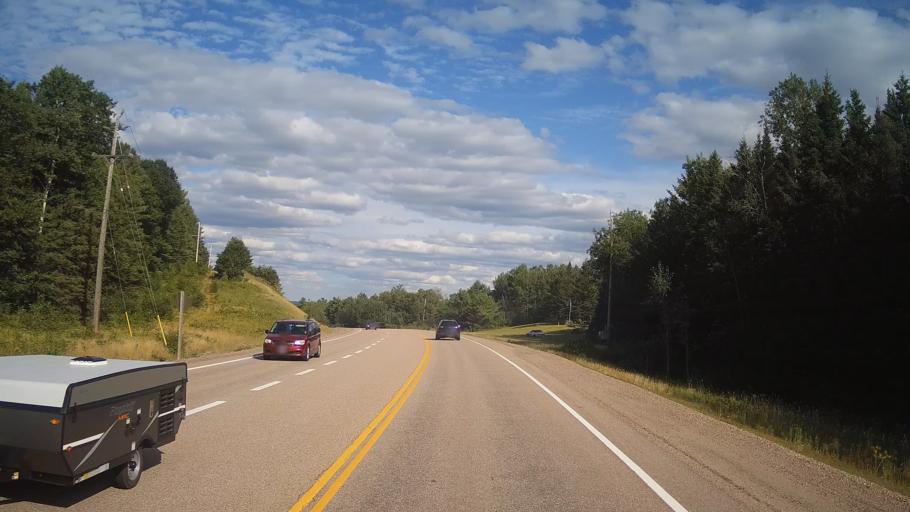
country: CA
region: Ontario
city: Mattawa
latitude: 46.2681
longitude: -79.0160
